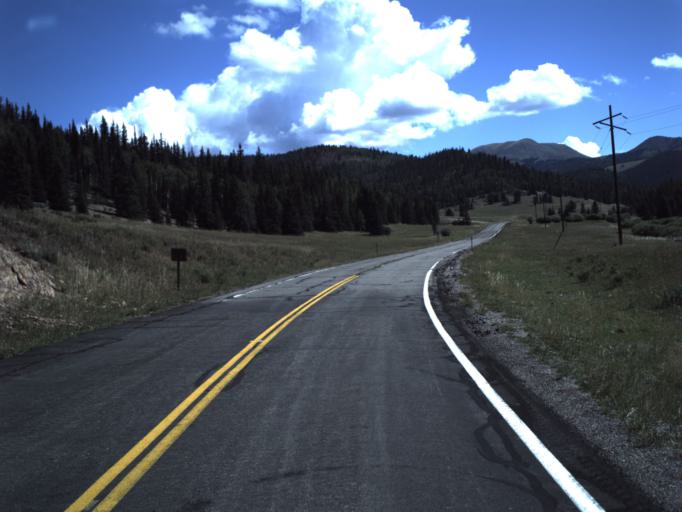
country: US
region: Utah
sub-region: Beaver County
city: Beaver
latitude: 38.2965
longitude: -112.4387
